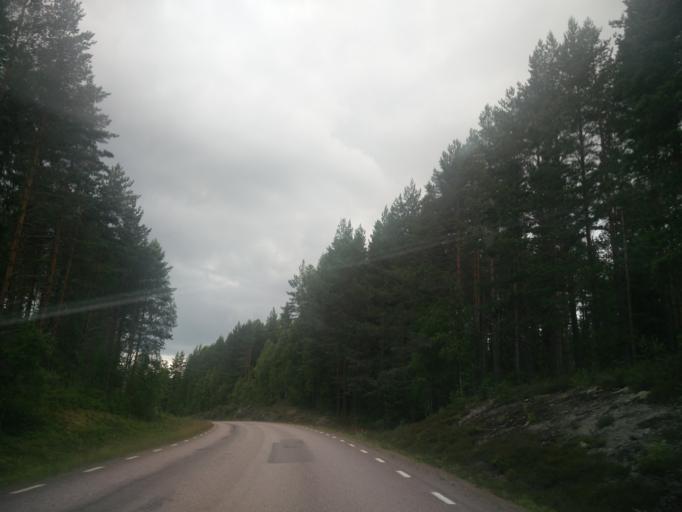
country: SE
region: Vaermland
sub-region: Arvika Kommun
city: Arvika
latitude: 59.9162
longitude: 12.6493
